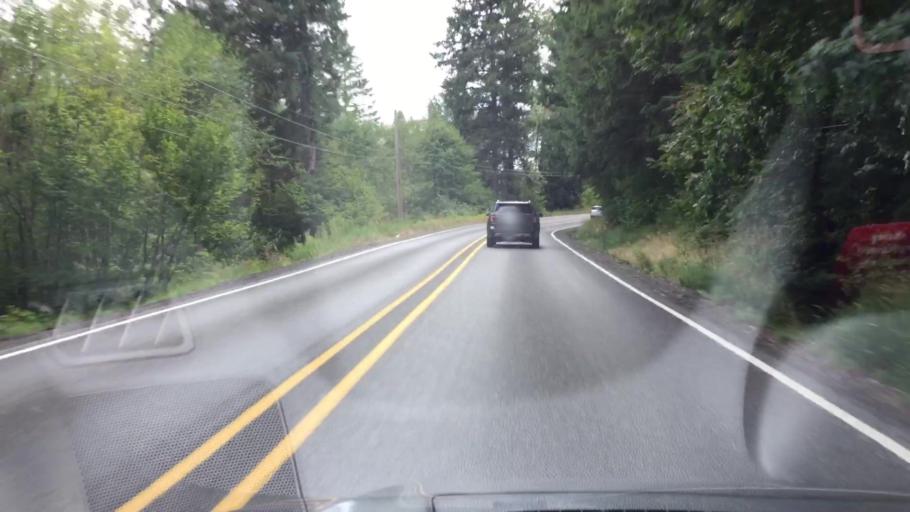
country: US
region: Washington
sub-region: Pierce County
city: Eatonville
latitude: 46.8425
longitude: -122.2479
